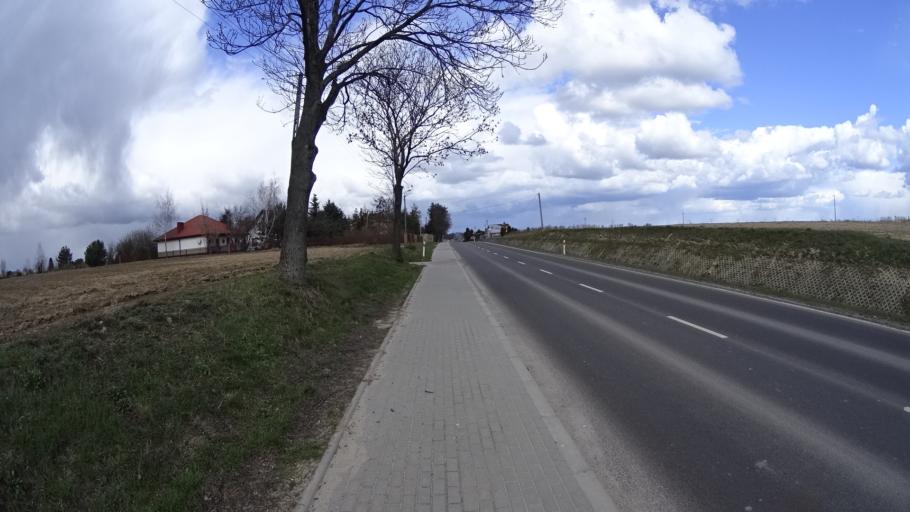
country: PL
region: Masovian Voivodeship
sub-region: Powiat warszawski zachodni
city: Jozefow
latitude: 52.2163
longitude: 20.6919
